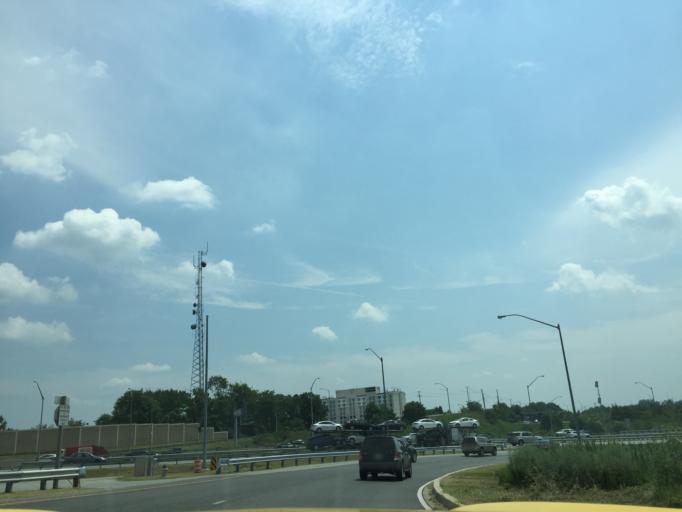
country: US
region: Maryland
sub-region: Prince George's County
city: Forest Heights
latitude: 38.8055
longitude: -76.9968
